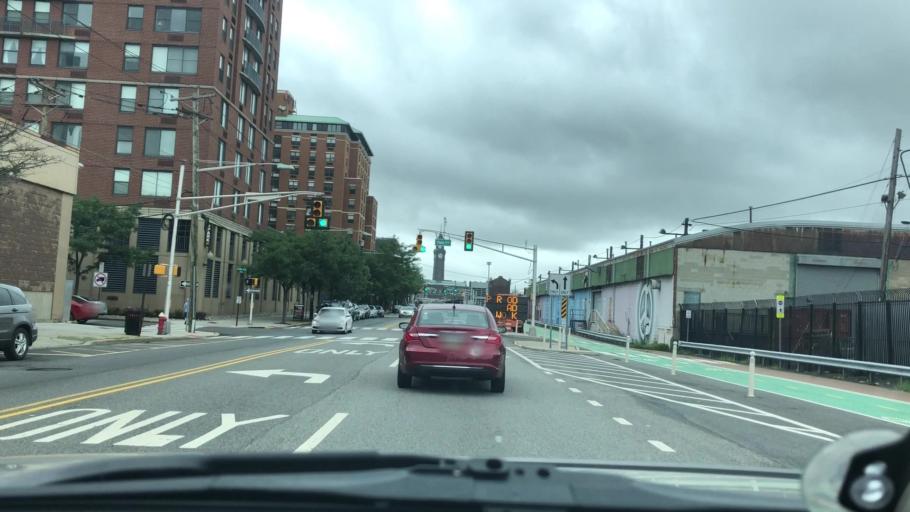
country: US
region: New Jersey
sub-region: Hudson County
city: Hoboken
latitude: 40.7361
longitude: -74.0346
